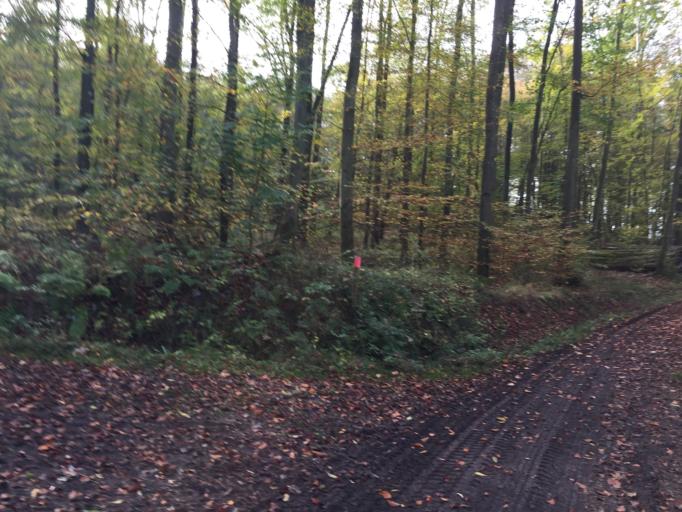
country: DE
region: Hesse
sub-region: Regierungsbezirk Giessen
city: Laubach
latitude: 50.5737
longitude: 8.9957
